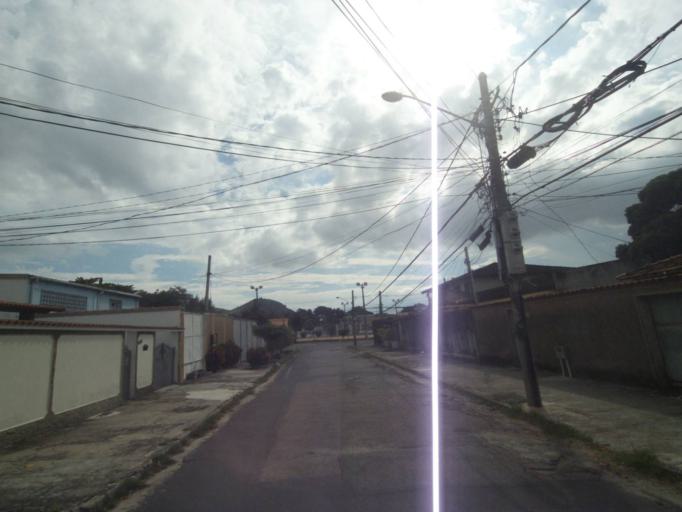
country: BR
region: Rio de Janeiro
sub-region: Nilopolis
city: Nilopolis
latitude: -22.8887
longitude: -43.3915
